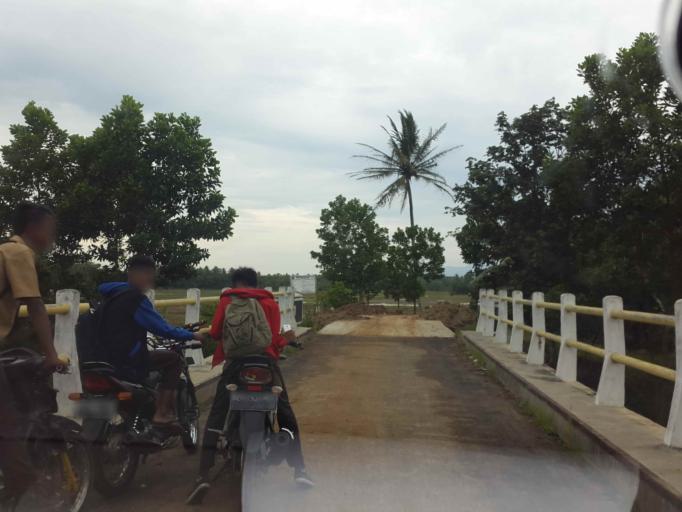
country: ID
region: Lampung
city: Jabung
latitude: -5.4758
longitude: 105.5610
